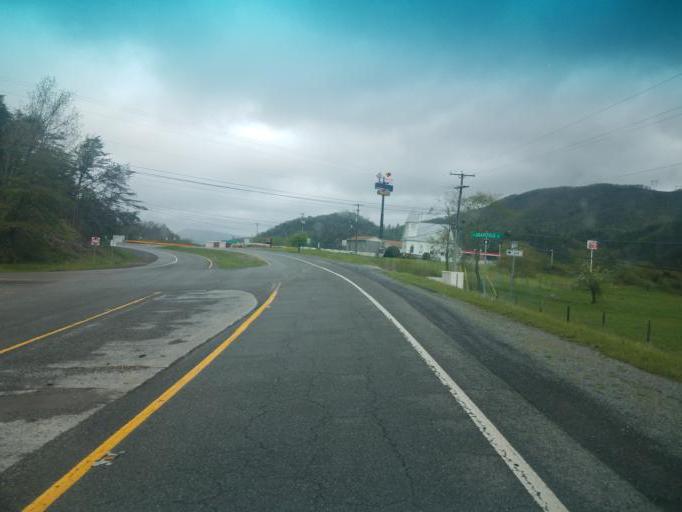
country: US
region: Virginia
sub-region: Bland County
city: Bland
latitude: 37.1765
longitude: -81.1427
